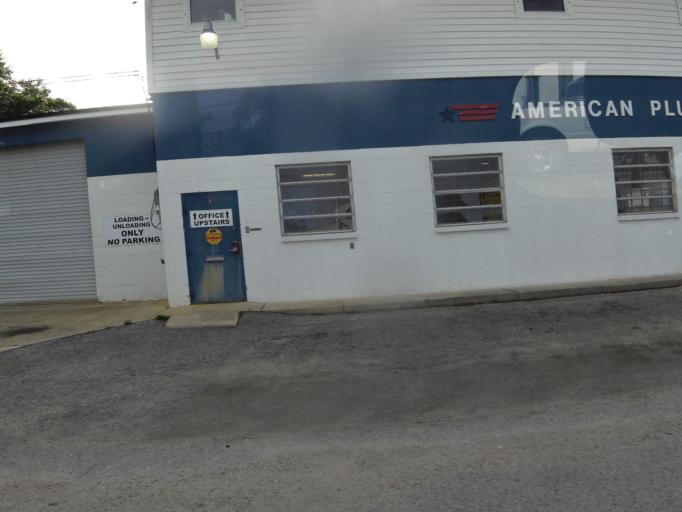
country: US
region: Florida
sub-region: Duval County
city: Jacksonville
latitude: 30.3332
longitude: -81.6010
